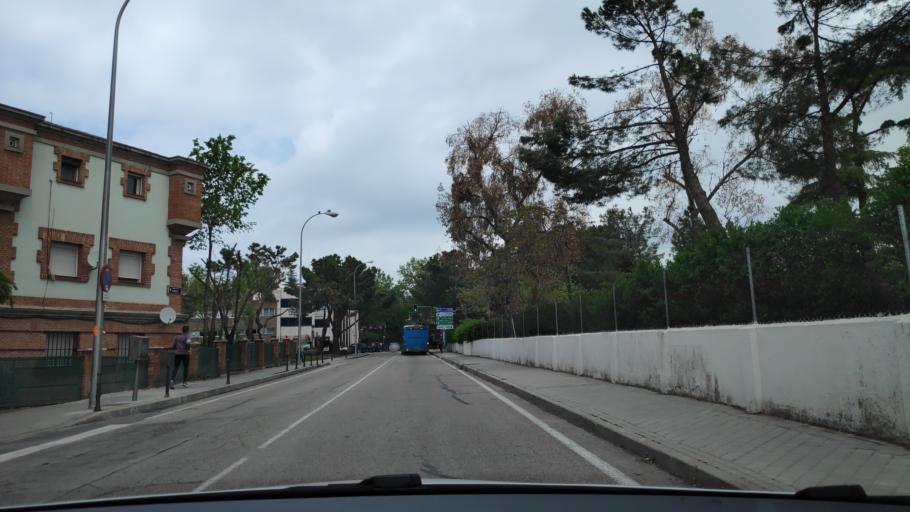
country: ES
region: Madrid
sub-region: Provincia de Madrid
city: Pozuelo de Alarcon
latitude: 40.4587
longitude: -3.7790
